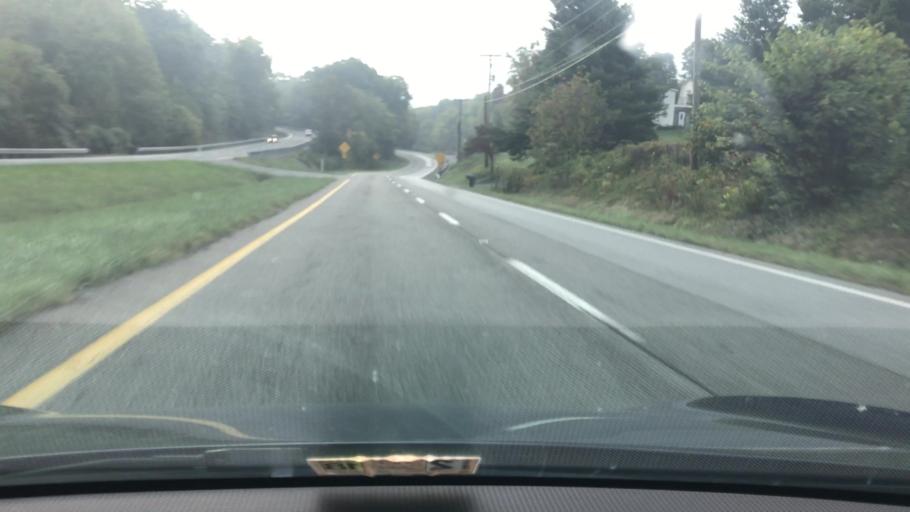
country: US
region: Virginia
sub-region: Botetourt County
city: Blue Ridge
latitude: 37.3907
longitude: -79.7428
